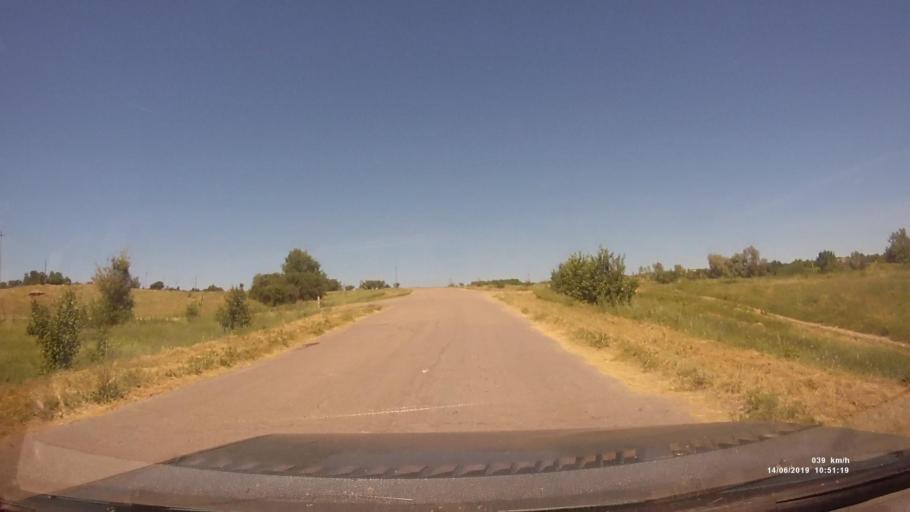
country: RU
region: Rostov
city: Kazanskaya
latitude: 49.8691
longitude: 41.3933
